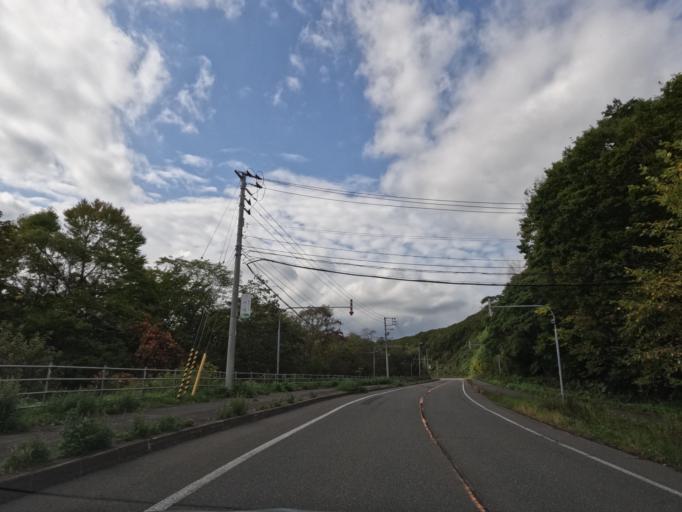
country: JP
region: Hokkaido
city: Chitose
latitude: 42.8144
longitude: 141.6016
